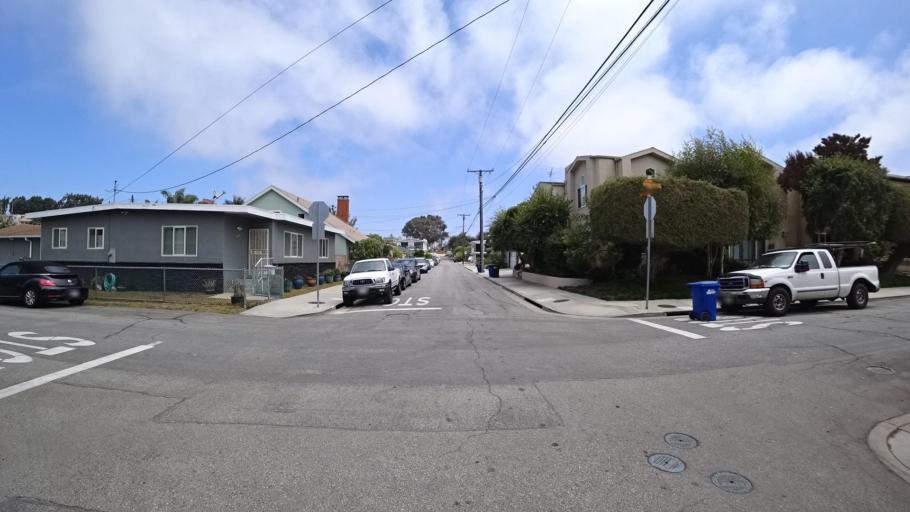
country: US
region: California
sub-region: Los Angeles County
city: Hermosa Beach
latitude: 33.8654
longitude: -118.3905
